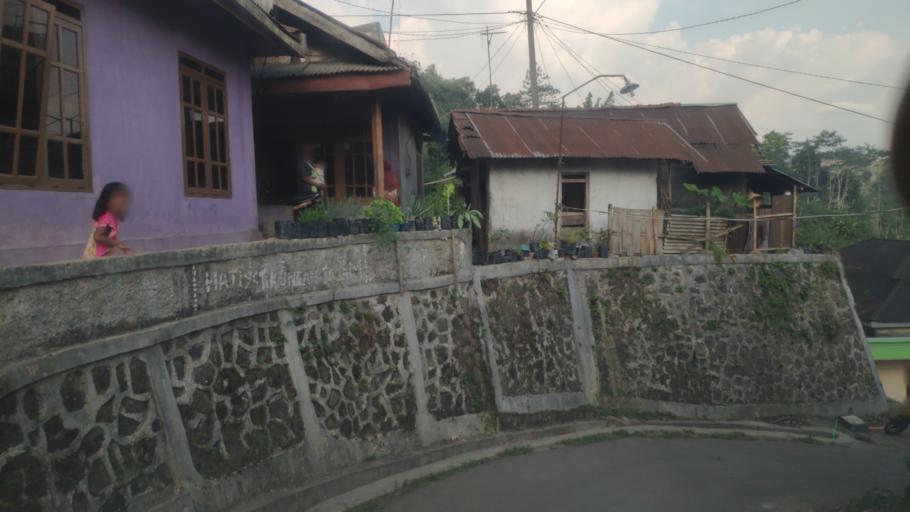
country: ID
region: Central Java
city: Buaran
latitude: -7.2537
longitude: 109.6760
